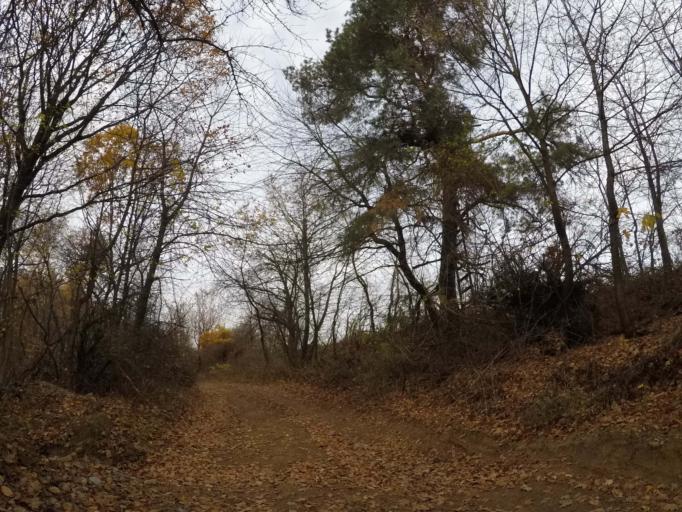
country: SK
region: Presovsky
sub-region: Okres Presov
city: Presov
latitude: 48.9248
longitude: 21.1435
